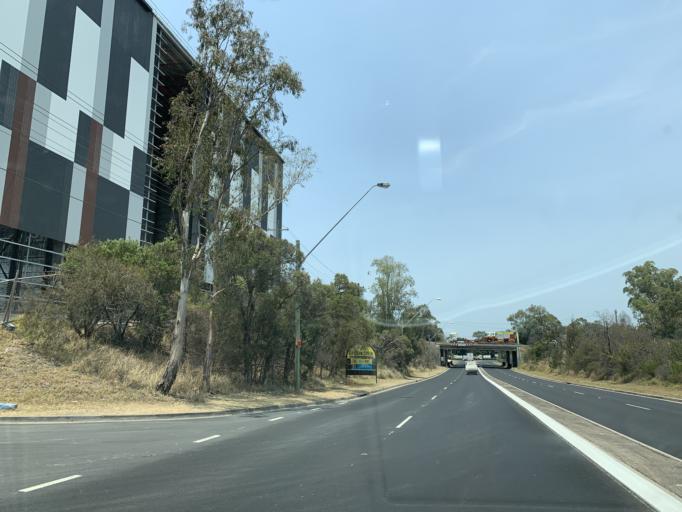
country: AU
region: New South Wales
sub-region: Blacktown
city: Doonside
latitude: -33.7995
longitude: 150.8704
